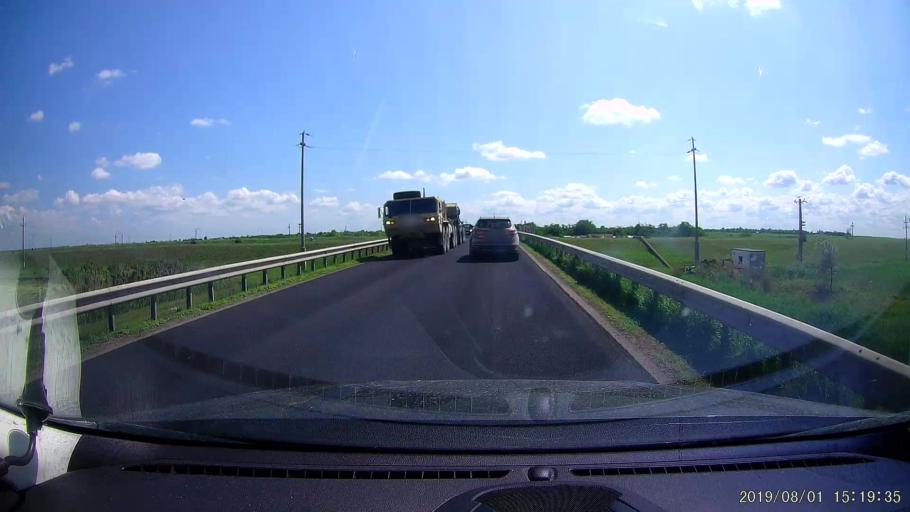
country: RO
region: Braila
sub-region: Comuna Unirea
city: Unirea
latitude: 45.0870
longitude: 27.8113
